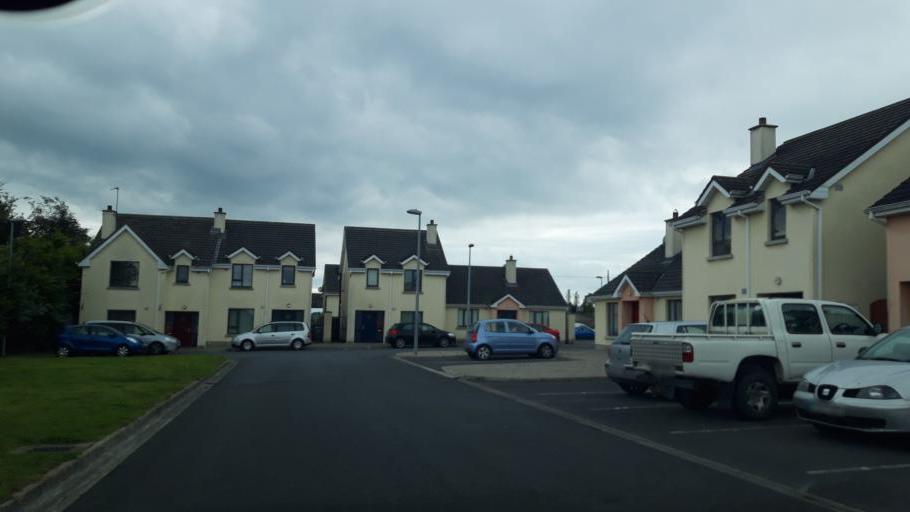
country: IE
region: Leinster
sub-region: Kilkenny
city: Ballyragget
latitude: 52.7918
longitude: -7.3299
